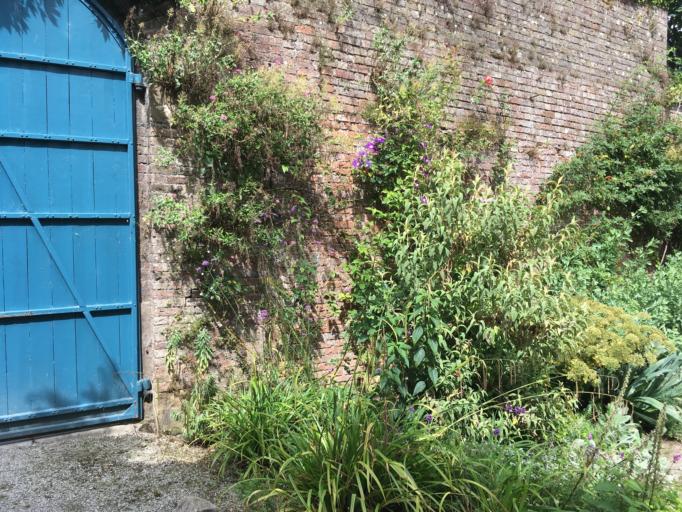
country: IE
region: Munster
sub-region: County Cork
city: Youghal
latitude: 52.1404
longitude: -7.9333
